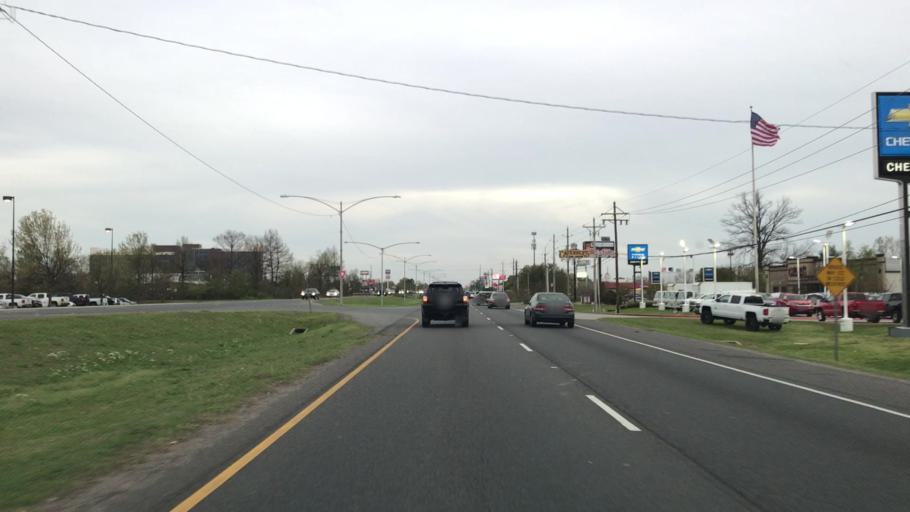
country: US
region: Louisiana
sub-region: Bossier Parish
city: Bossier City
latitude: 32.4369
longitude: -93.7149
